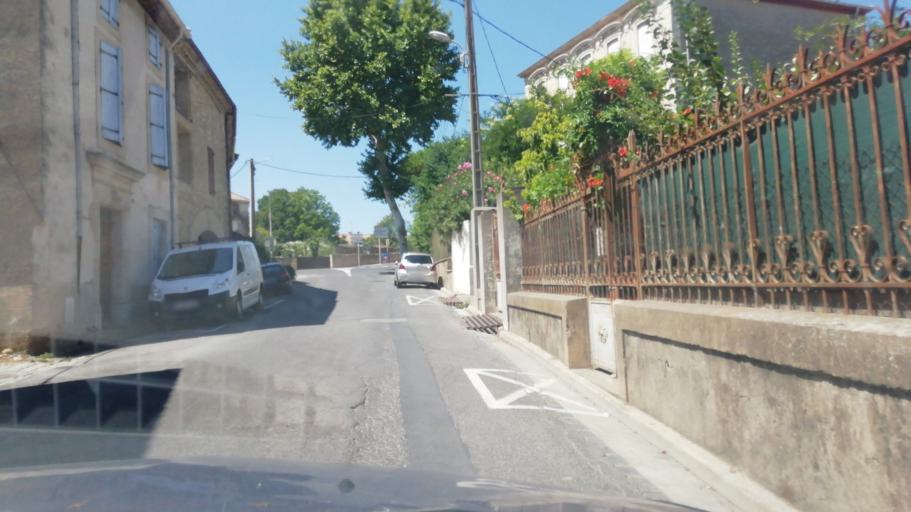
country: FR
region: Languedoc-Roussillon
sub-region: Departement de l'Herault
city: Capestang
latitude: 43.3302
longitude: 3.0431
